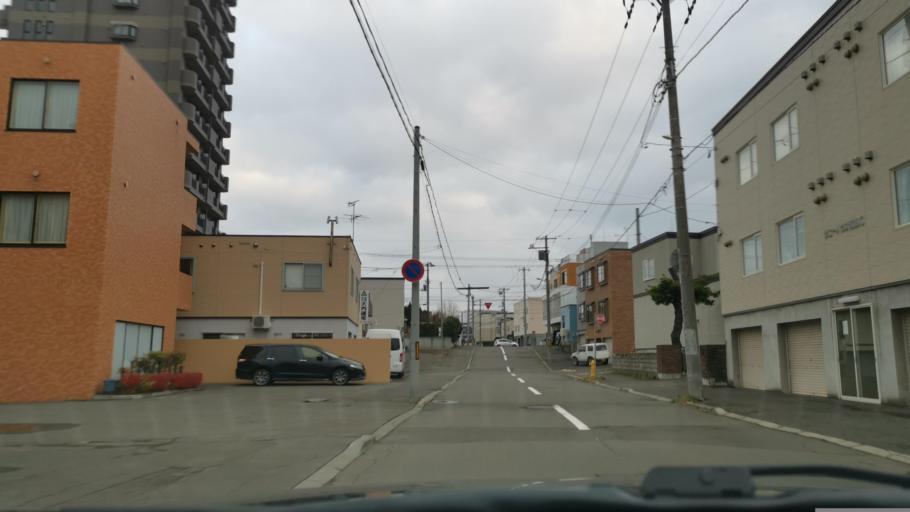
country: JP
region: Hokkaido
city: Sapporo
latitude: 43.0458
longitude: 141.4041
